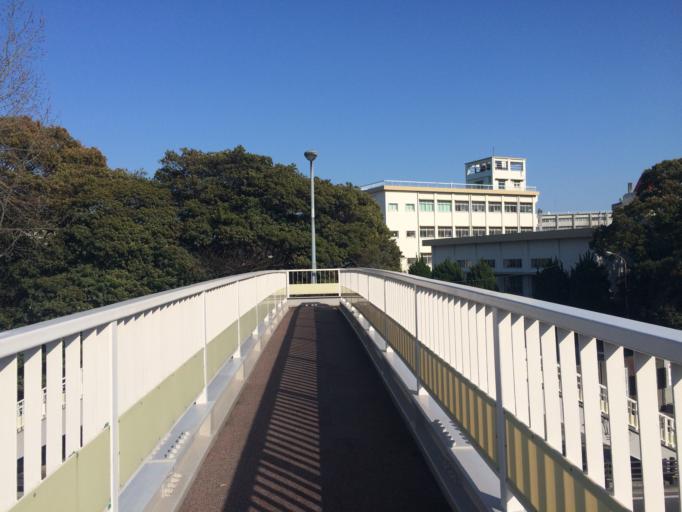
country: JP
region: Fukuoka
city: Fukuoka-shi
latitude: 33.6271
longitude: 130.4215
